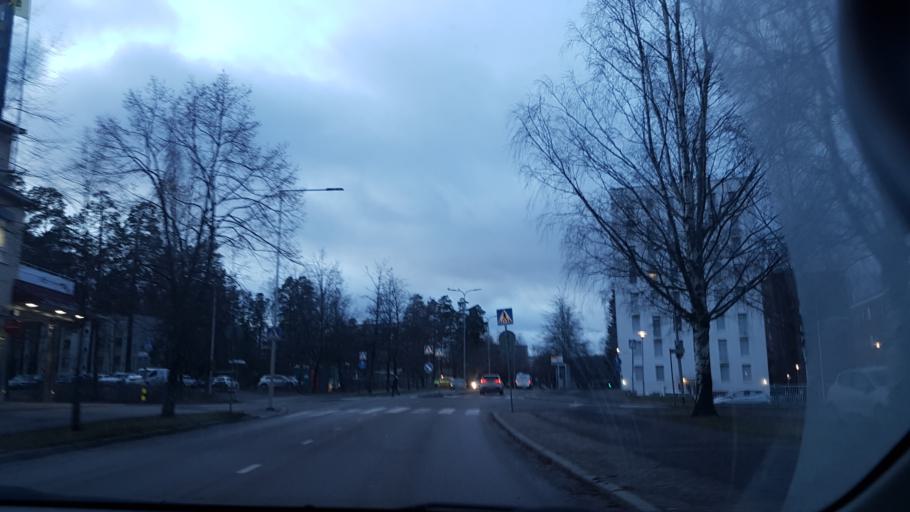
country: FI
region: Uusimaa
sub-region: Helsinki
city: Vantaa
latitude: 60.2804
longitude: 25.1092
